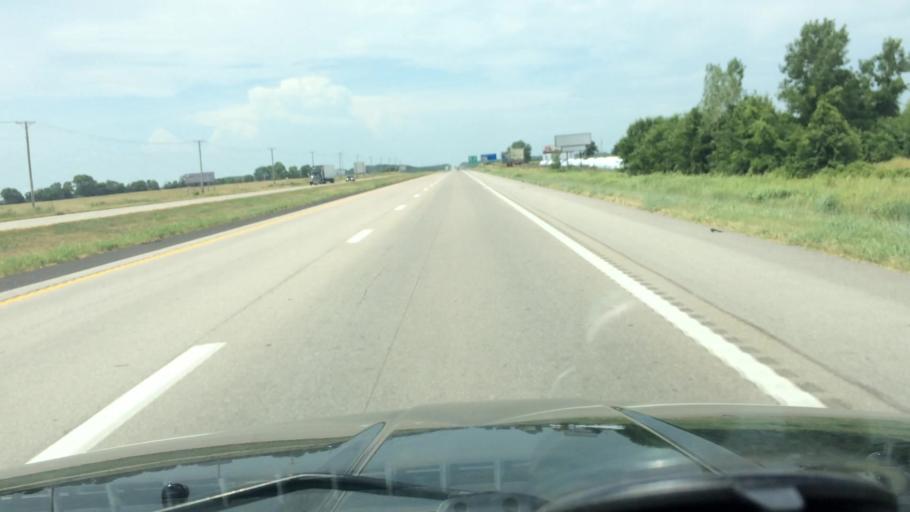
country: US
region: Missouri
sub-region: Polk County
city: Bolivar
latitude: 37.5996
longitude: -93.4374
